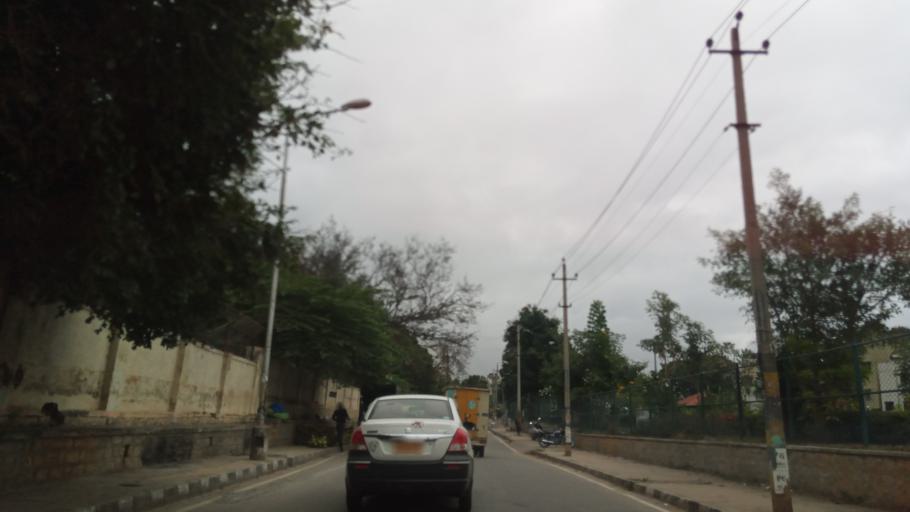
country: IN
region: Karnataka
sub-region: Bangalore Urban
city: Bangalore
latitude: 12.9348
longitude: 77.5393
